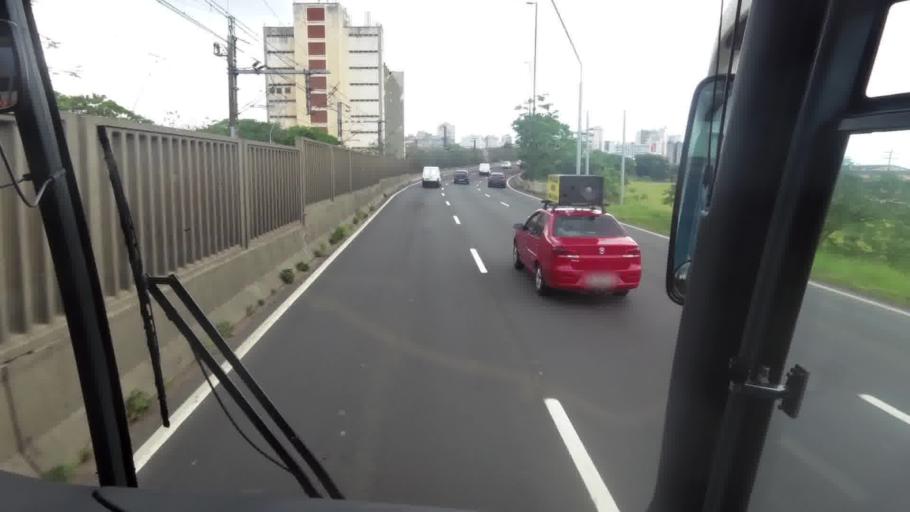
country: BR
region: Rio Grande do Sul
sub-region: Porto Alegre
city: Porto Alegre
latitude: -30.0195
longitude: -51.2160
